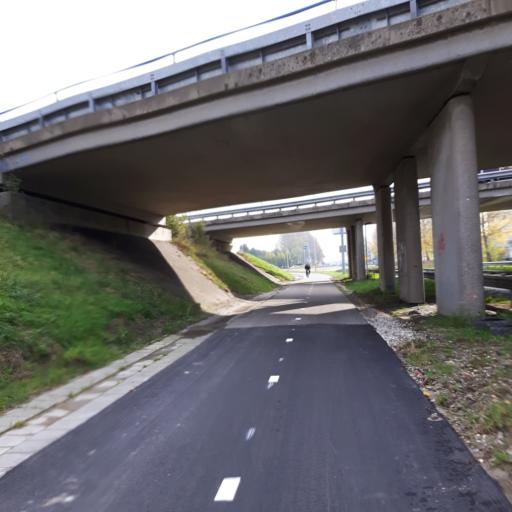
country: NL
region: Zeeland
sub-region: Gemeente Goes
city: Goes
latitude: 51.4836
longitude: 3.8176
